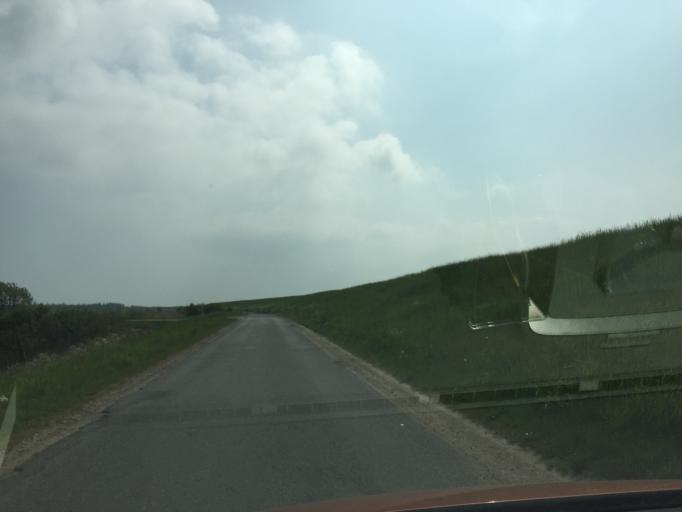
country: DK
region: South Denmark
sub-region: Esbjerg Kommune
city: Ribe
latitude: 55.3029
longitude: 8.6602
